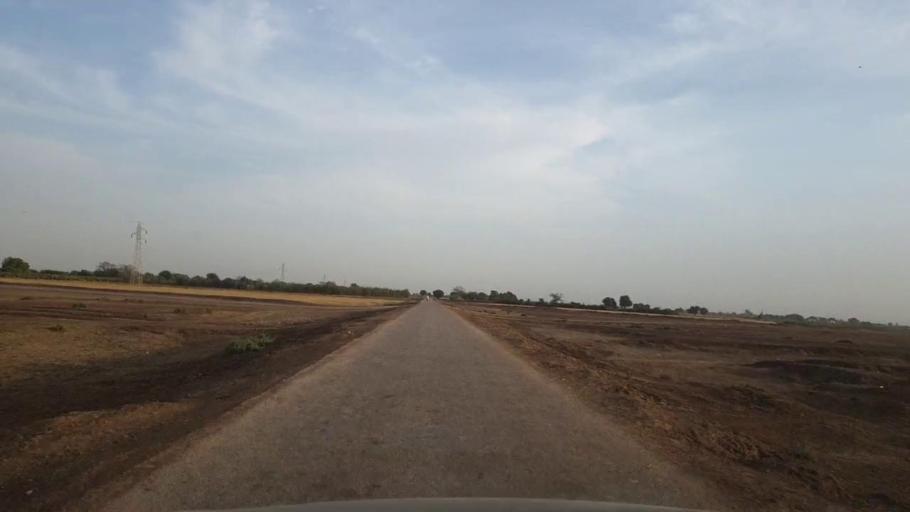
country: PK
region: Sindh
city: Kunri
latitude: 25.1696
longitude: 69.5447
